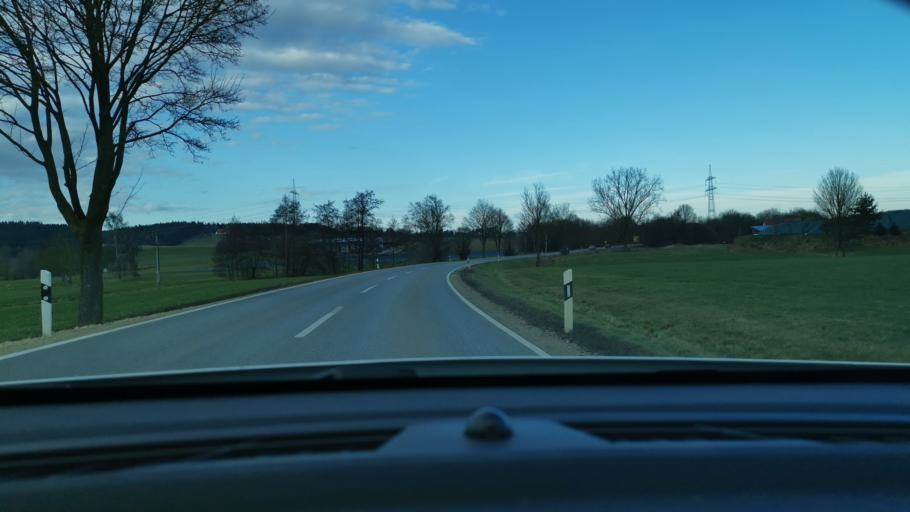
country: DE
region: Bavaria
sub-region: Swabia
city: Petersdorf
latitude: 48.5076
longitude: 11.0145
